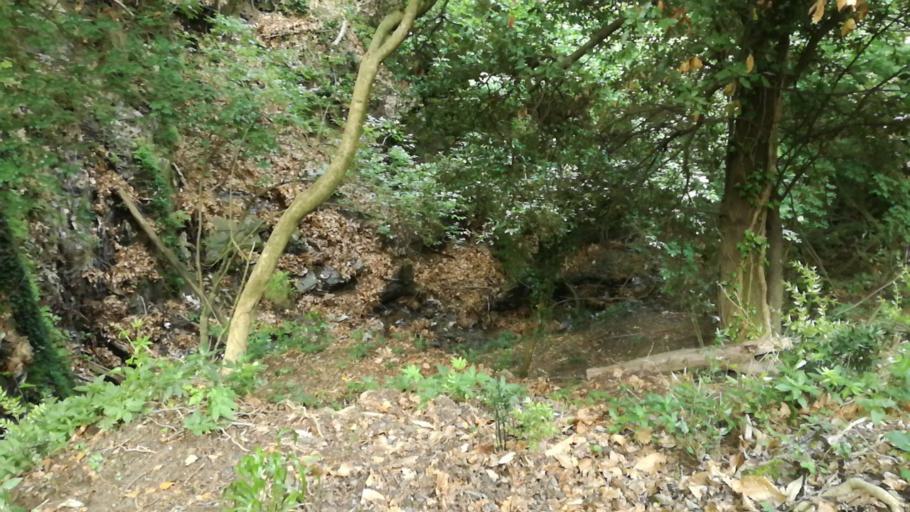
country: IT
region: Liguria
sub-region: Provincia di Genova
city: Genoa
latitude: 44.4310
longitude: 8.9063
